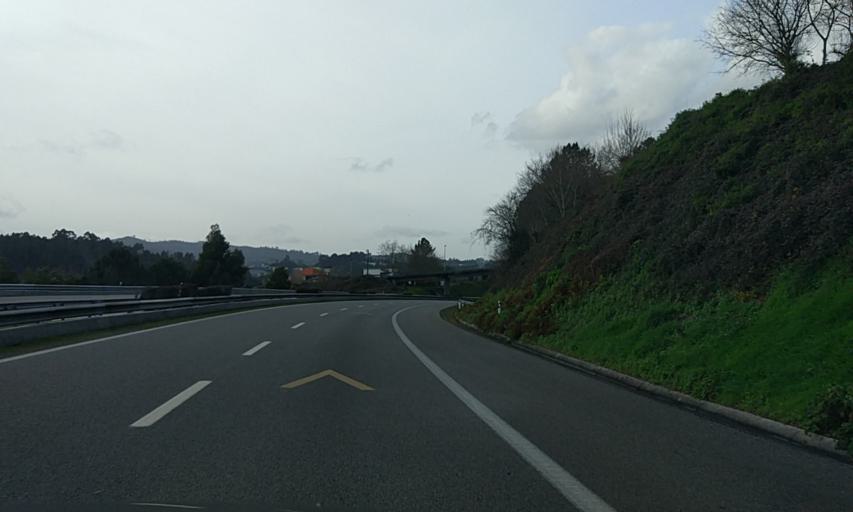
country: PT
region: Porto
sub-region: Marco de Canaveses
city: Marco de Canavezes
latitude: 41.2220
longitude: -8.1627
